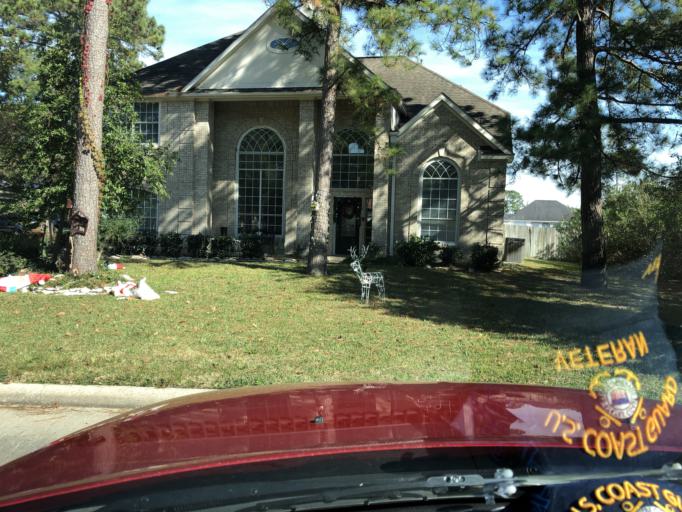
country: US
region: Texas
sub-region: Harris County
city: Tomball
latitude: 30.0195
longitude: -95.5507
